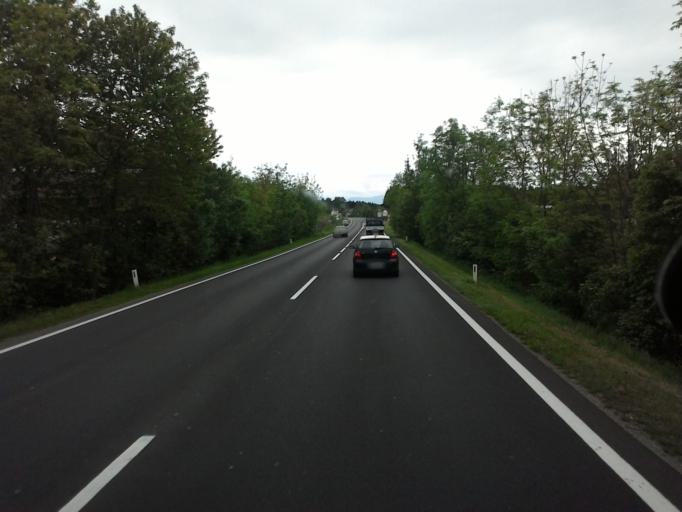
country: AT
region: Upper Austria
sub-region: Wels-Land
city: Sattledt
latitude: 48.0800
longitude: 14.0472
